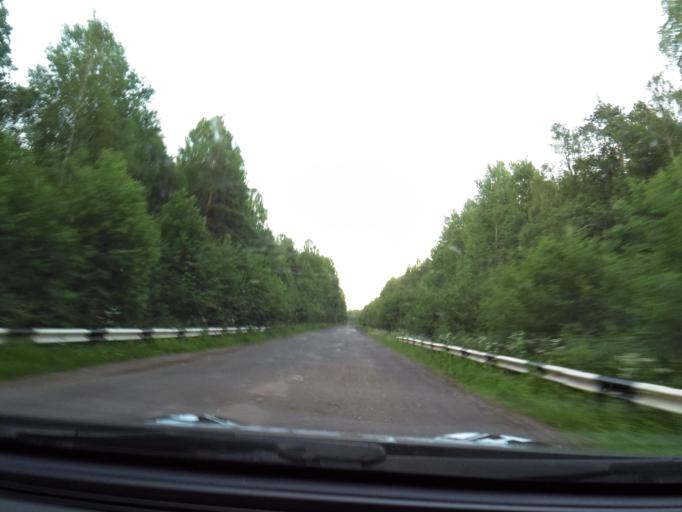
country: RU
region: Leningrad
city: Voznesen'ye
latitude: 60.8406
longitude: 35.6353
